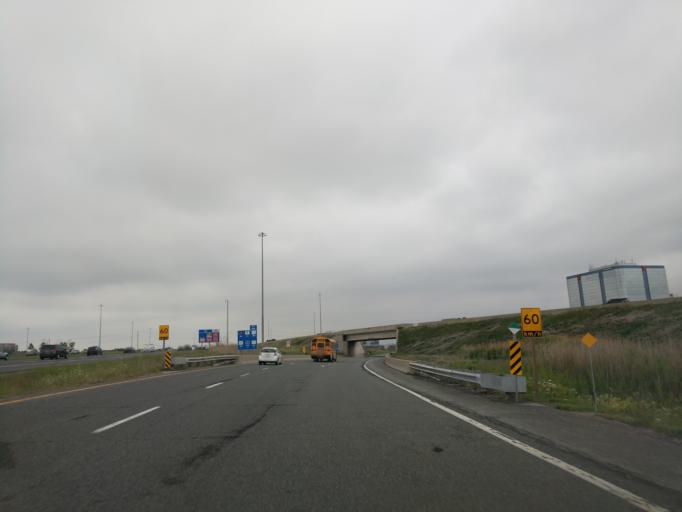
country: CA
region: Ontario
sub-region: York
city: Richmond Hill
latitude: 43.8426
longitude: -79.3690
